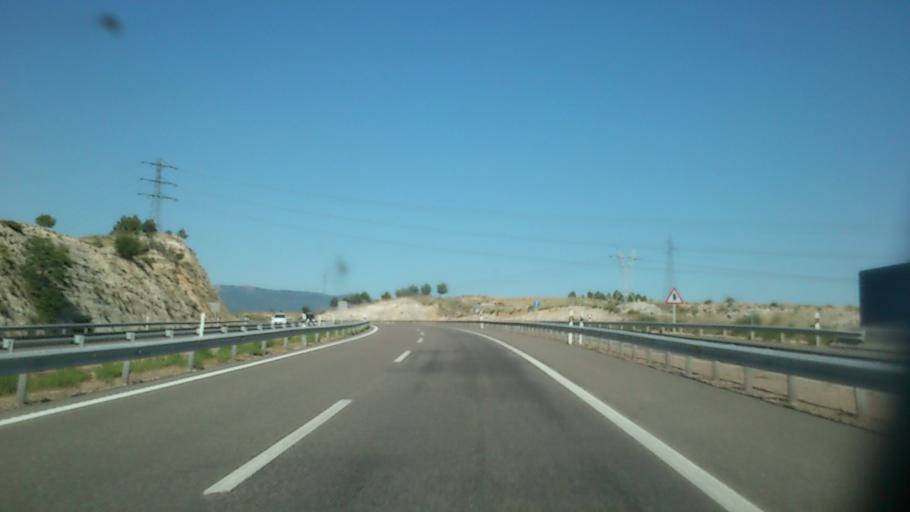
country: ES
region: Aragon
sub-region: Provincia de Zaragoza
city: Calatayud
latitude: 41.3340
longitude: -1.6419
